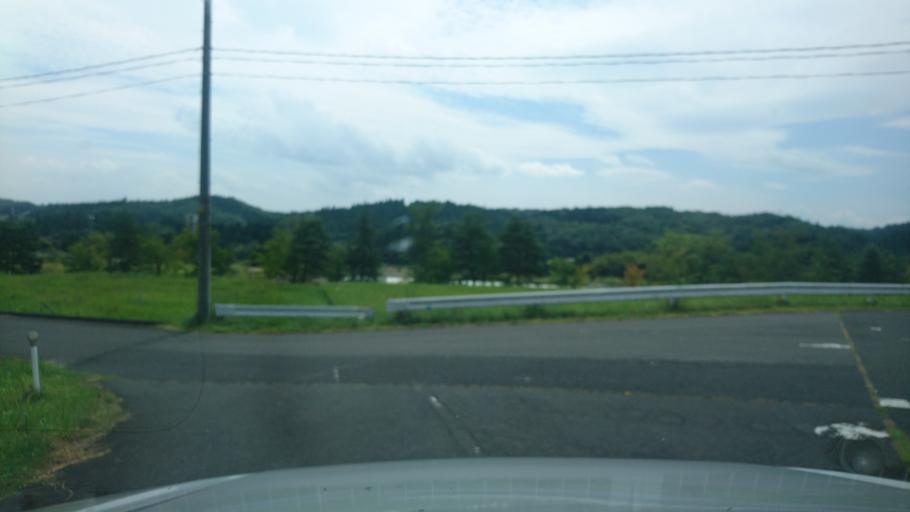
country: JP
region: Iwate
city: Ichinoseki
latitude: 38.8078
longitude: 140.9260
